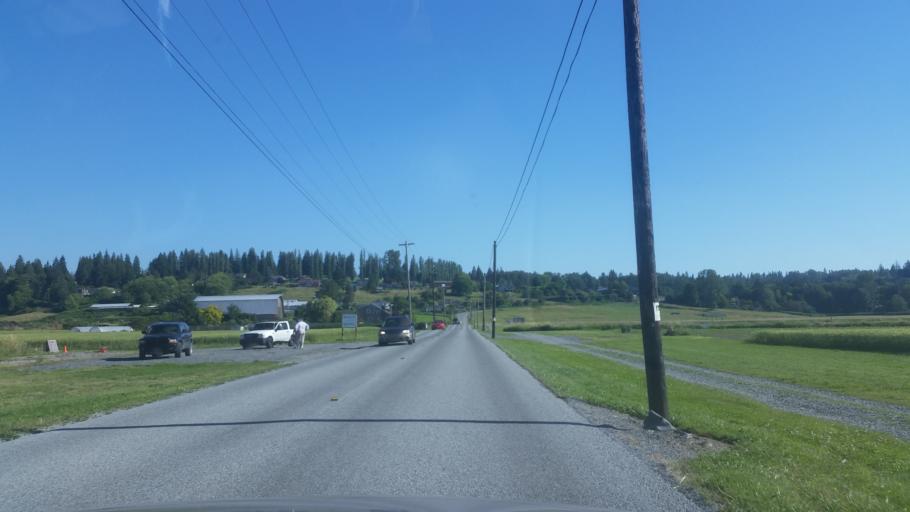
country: US
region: Washington
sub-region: Snohomish County
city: Snohomish
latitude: 47.8832
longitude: -122.0990
